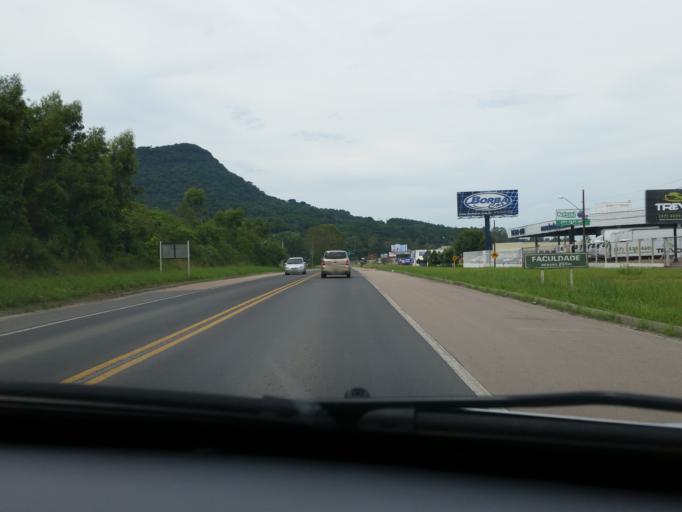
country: BR
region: Santa Catarina
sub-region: Rio Do Sul
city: Rio do Sul
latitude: -27.1953
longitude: -49.6257
